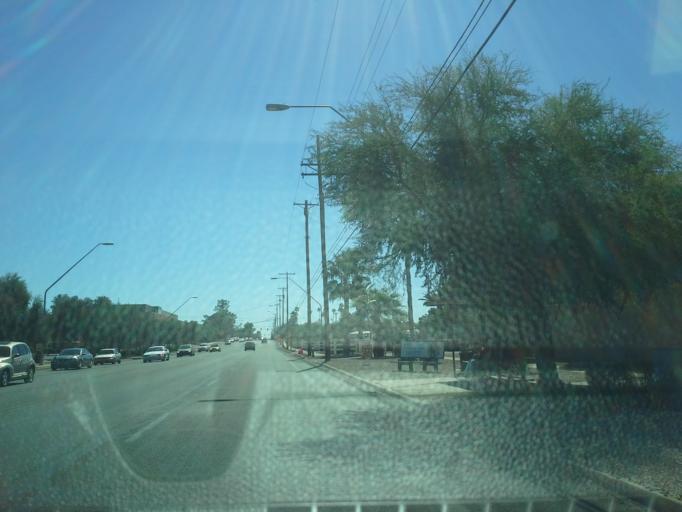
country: US
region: Arizona
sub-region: Pima County
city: Catalina Foothills
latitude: 32.2792
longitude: -110.9439
